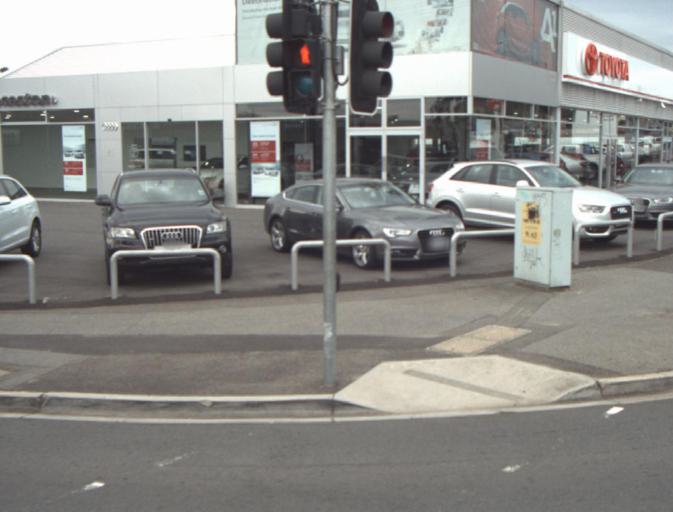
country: AU
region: Tasmania
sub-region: Launceston
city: East Launceston
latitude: -41.4649
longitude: 147.1589
